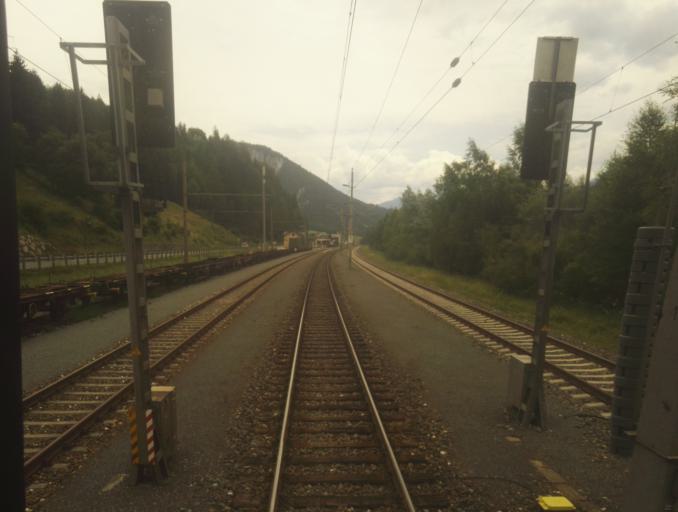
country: AT
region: Salzburg
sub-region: Politischer Bezirk Sankt Johann im Pongau
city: Forstau
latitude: 47.4045
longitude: 13.5651
